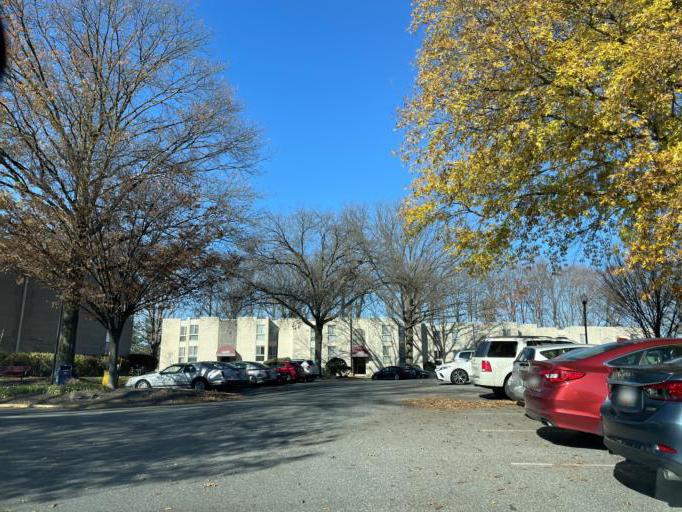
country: US
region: Maryland
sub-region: Baltimore County
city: Lutherville
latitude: 39.3770
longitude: -76.6608
